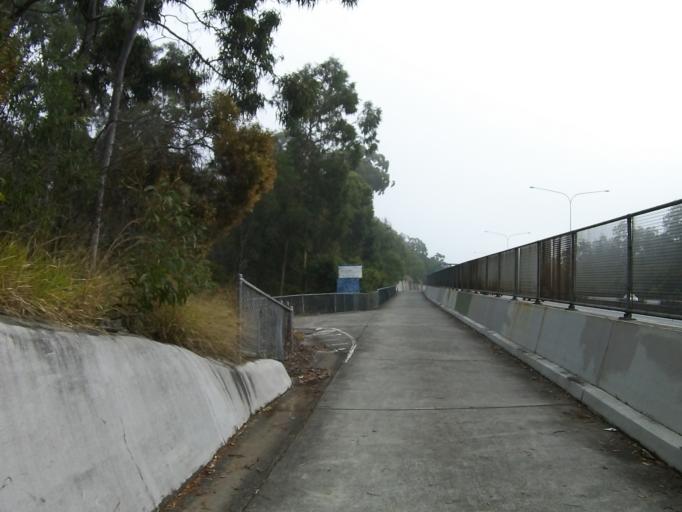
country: AU
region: Queensland
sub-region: Brisbane
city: Nathan
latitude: -27.5442
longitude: 153.0616
